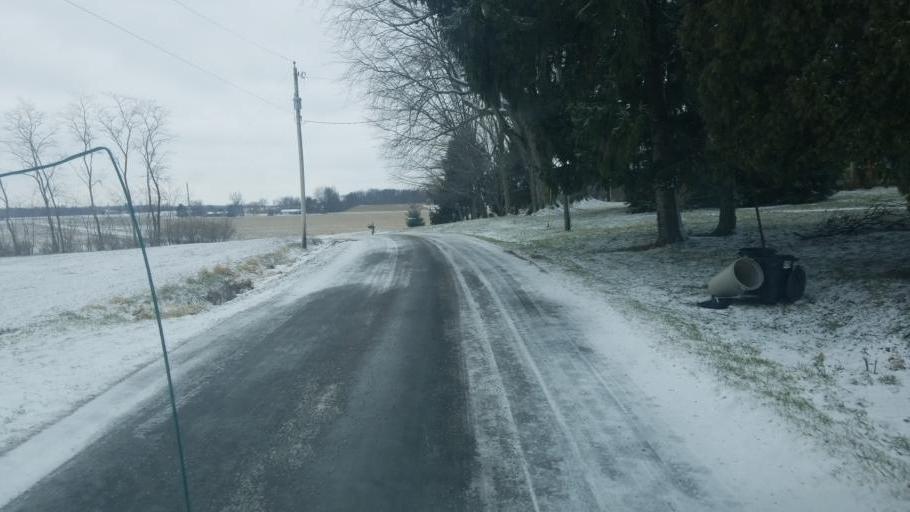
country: US
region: Ohio
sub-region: Delaware County
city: Sunbury
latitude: 40.2375
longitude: -82.7738
